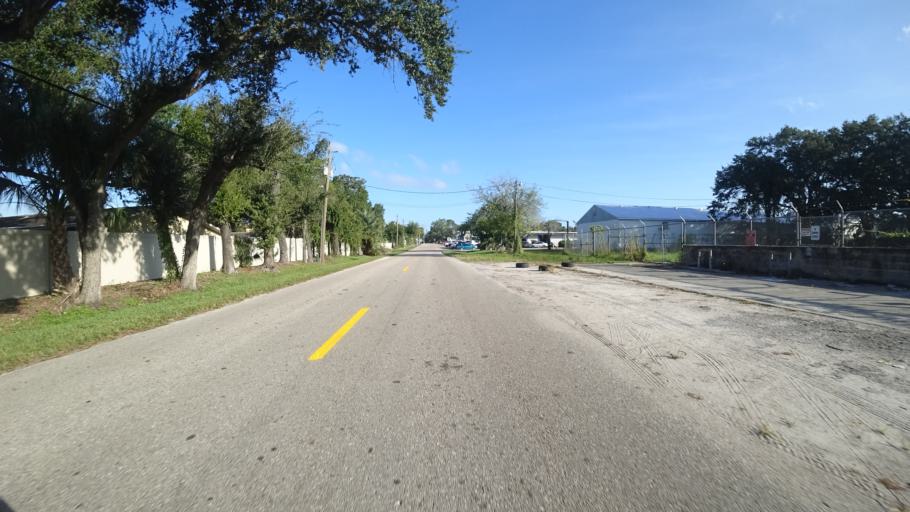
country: US
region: Florida
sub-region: Manatee County
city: West Samoset
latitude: 27.4709
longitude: -82.5651
